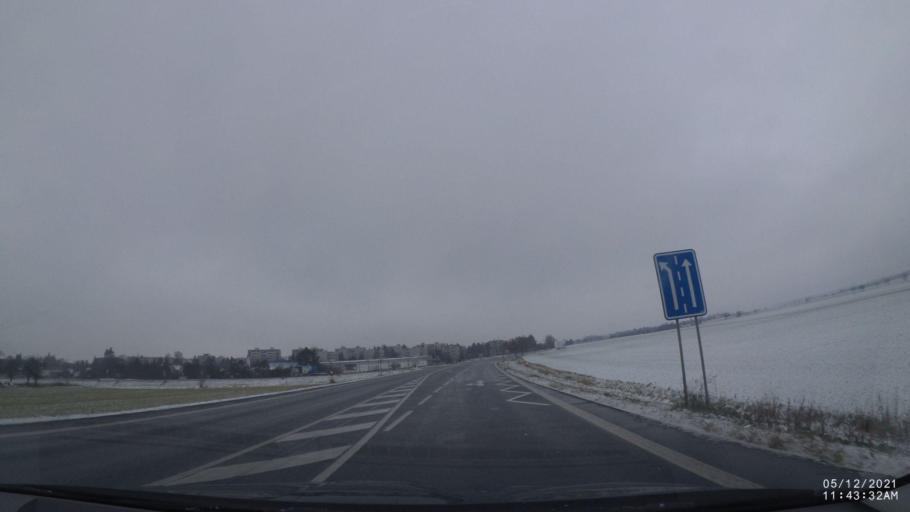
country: CZ
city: Dobruska
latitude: 50.2872
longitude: 16.1708
